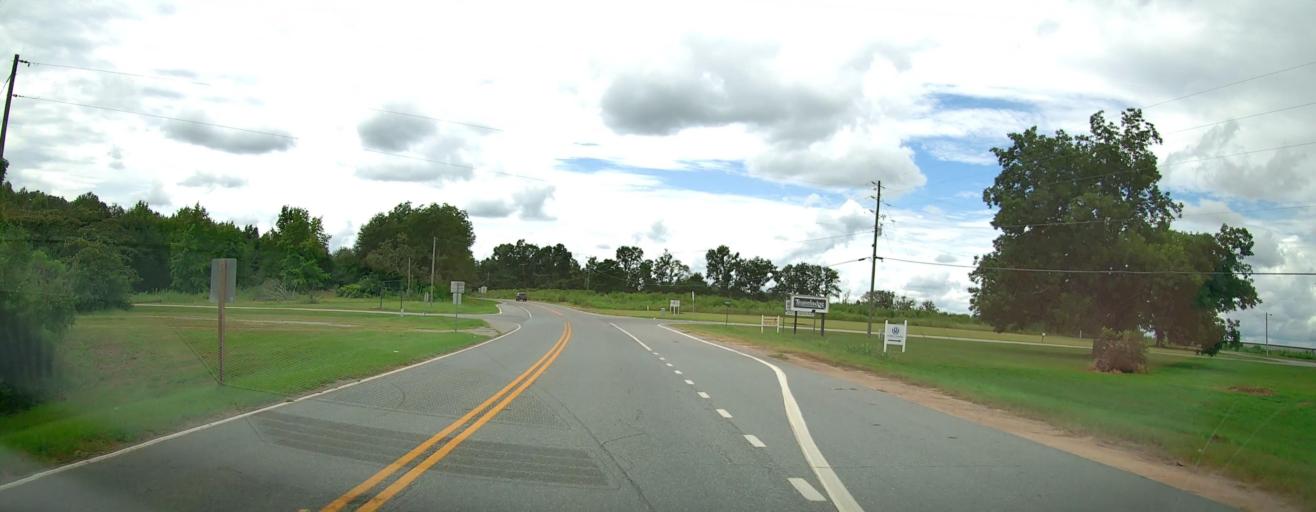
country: US
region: Georgia
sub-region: Dooly County
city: Unadilla
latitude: 32.2605
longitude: -83.7517
